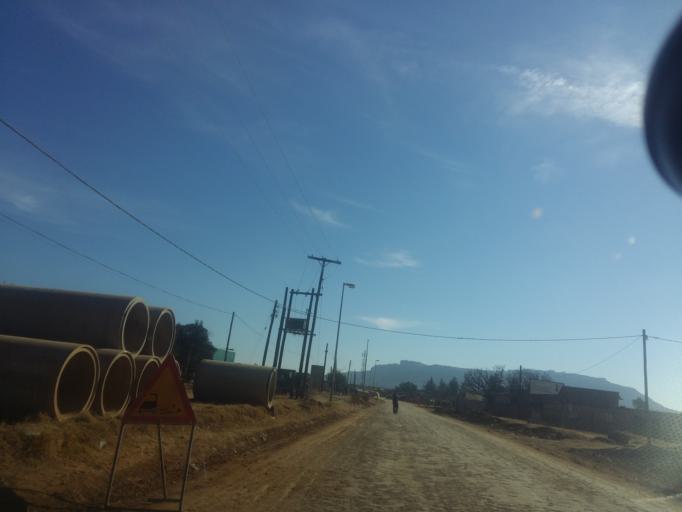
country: LS
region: Maseru
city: Maseru
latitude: -29.3687
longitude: 27.5221
